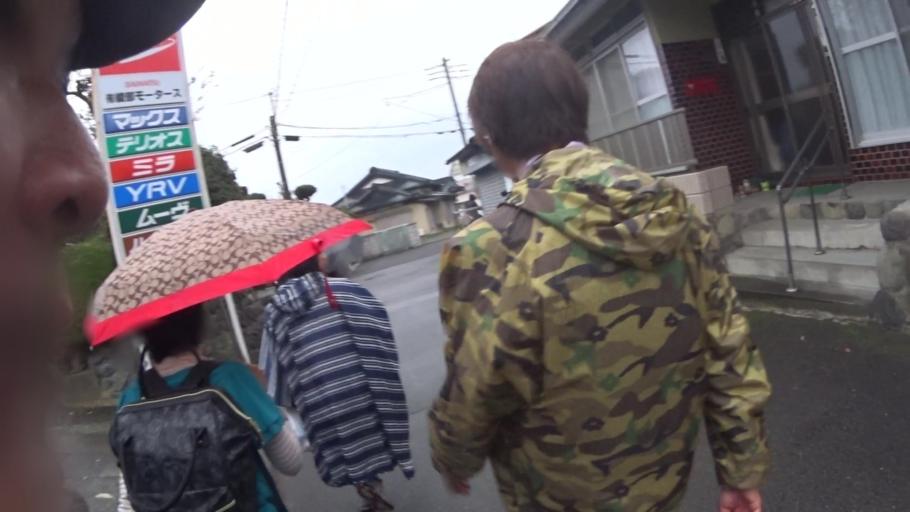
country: JP
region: Kanagawa
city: Hadano
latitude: 35.3677
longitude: 139.2216
